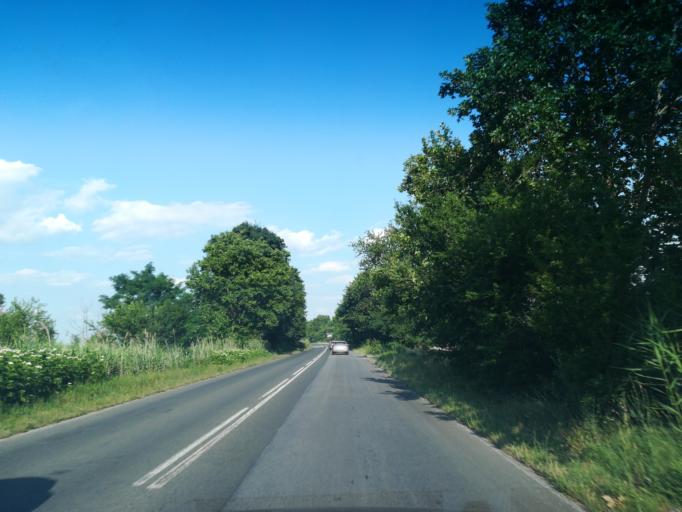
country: BG
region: Plovdiv
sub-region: Obshtina Sadovo
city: Sadovo
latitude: 42.1468
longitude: 24.8437
